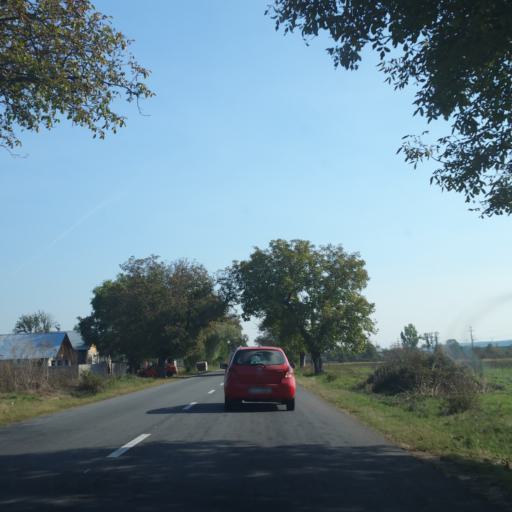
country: RO
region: Arges
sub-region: Comuna Merisani
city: Merisani
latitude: 45.0063
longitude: 24.7279
